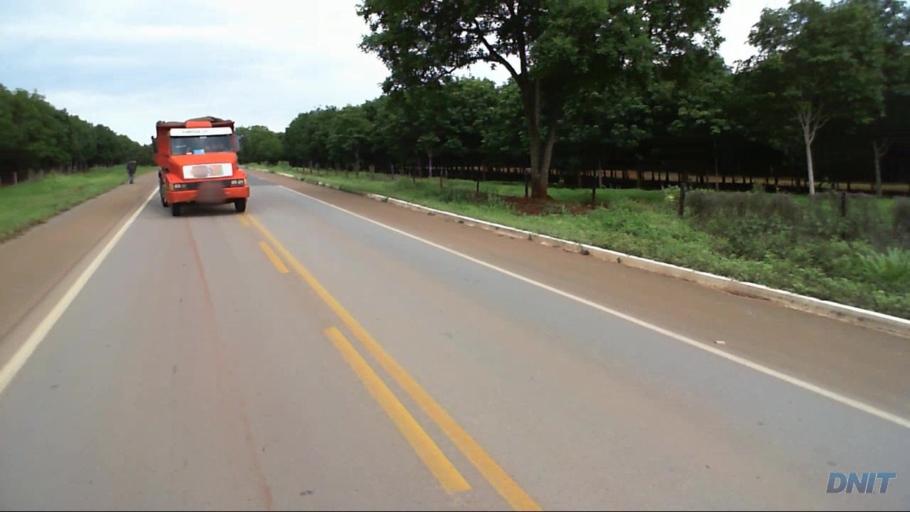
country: BR
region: Goias
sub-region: Barro Alto
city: Barro Alto
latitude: -14.8798
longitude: -48.9907
